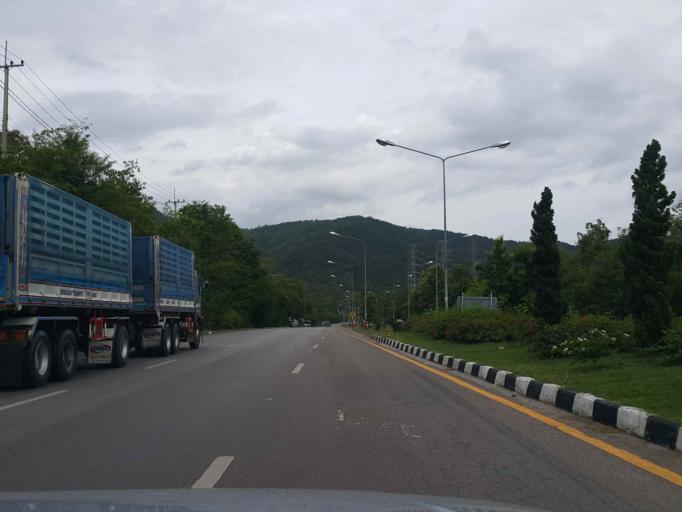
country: TH
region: Lampang
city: Lampang
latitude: 18.2557
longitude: 99.5497
